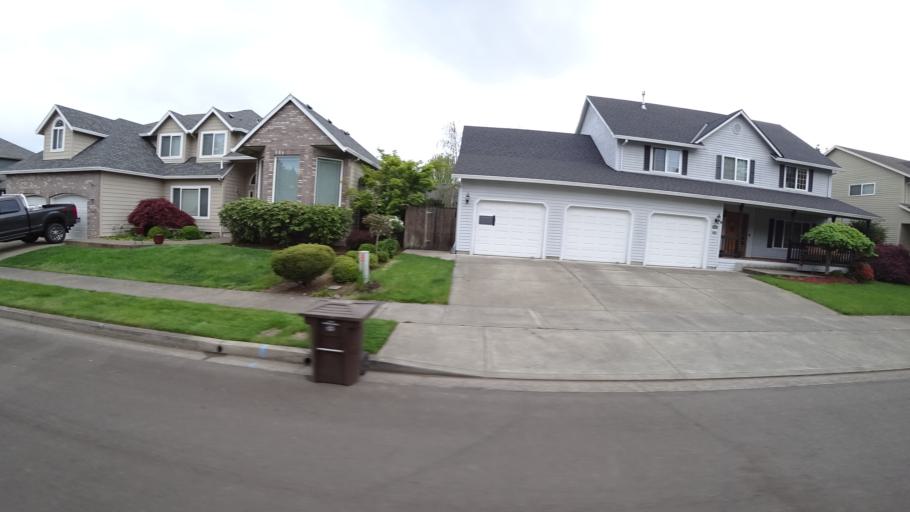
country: US
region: Oregon
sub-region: Washington County
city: Hillsboro
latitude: 45.5454
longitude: -122.9749
